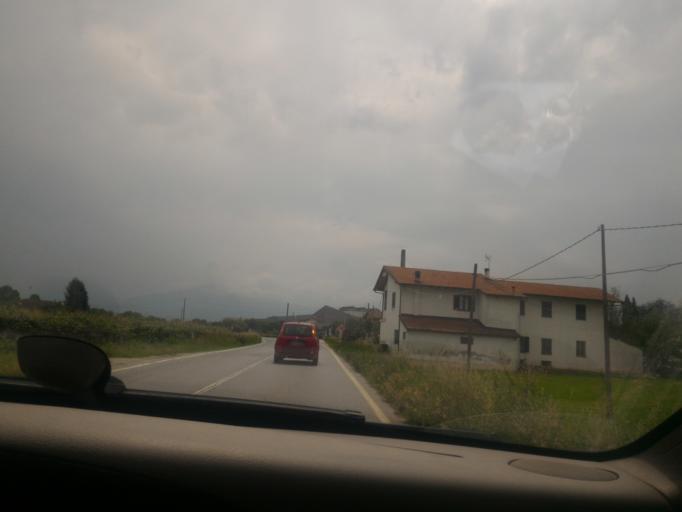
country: IT
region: Piedmont
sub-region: Provincia di Cuneo
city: Roata Rossi
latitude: 44.4294
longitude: 7.5447
